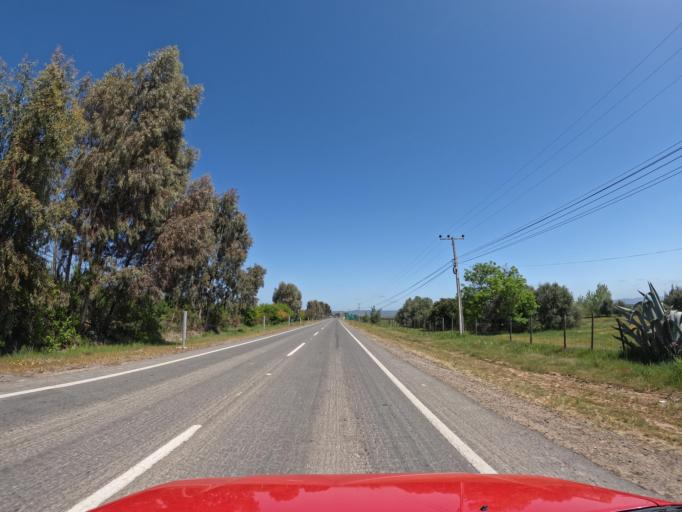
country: CL
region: O'Higgins
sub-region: Provincia de Colchagua
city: Santa Cruz
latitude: -34.7343
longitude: -71.6924
